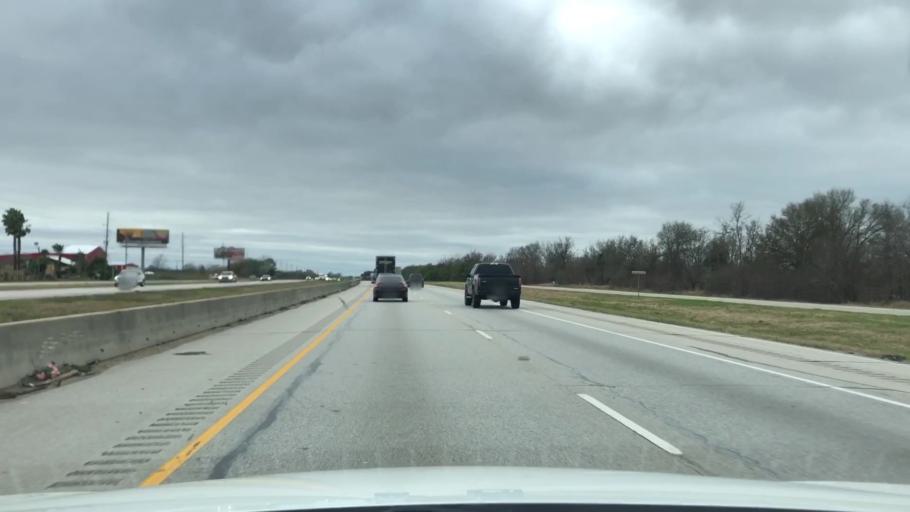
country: US
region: Texas
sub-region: Austin County
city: Sealy
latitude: 29.7747
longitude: -96.0837
